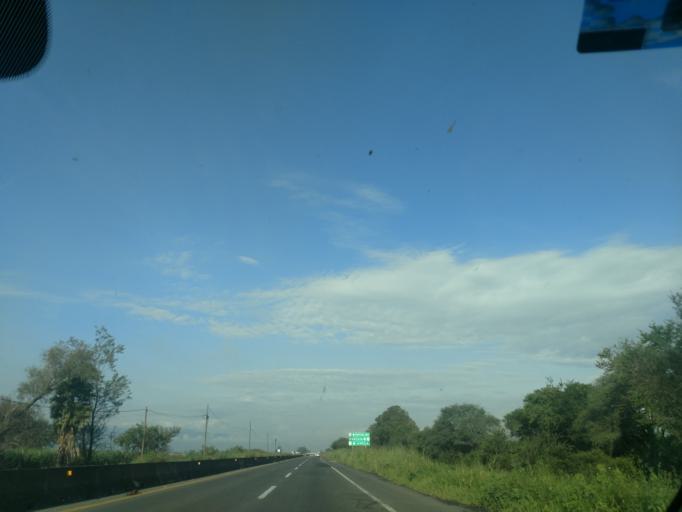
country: MX
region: Jalisco
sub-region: Ameca
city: Los Pocitos
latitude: 20.5356
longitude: -103.9524
